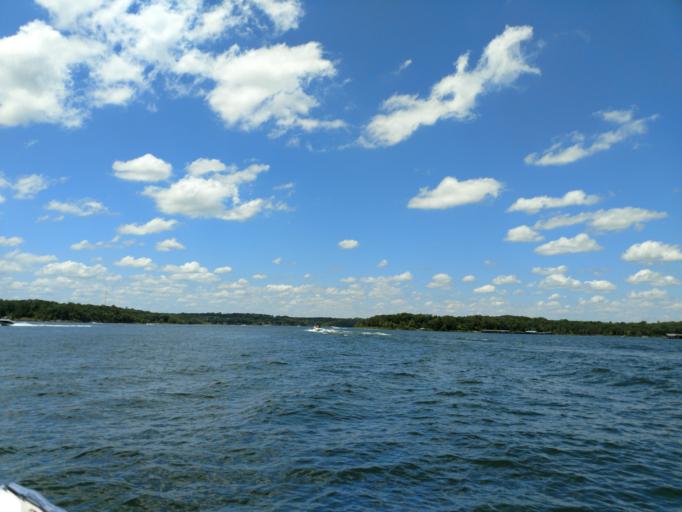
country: US
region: Missouri
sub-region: Barry County
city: Shell Knob
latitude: 36.5894
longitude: -93.5593
